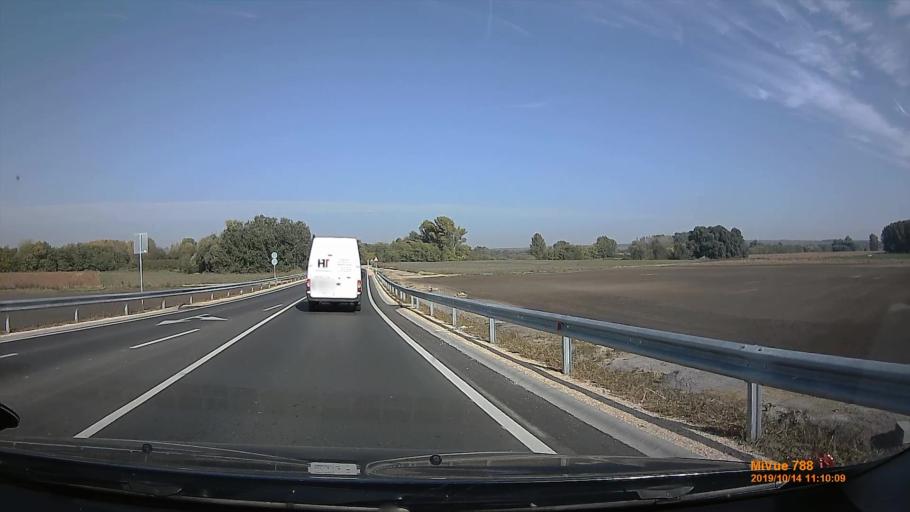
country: HU
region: Pest
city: Peteri
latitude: 47.3732
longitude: 19.4227
